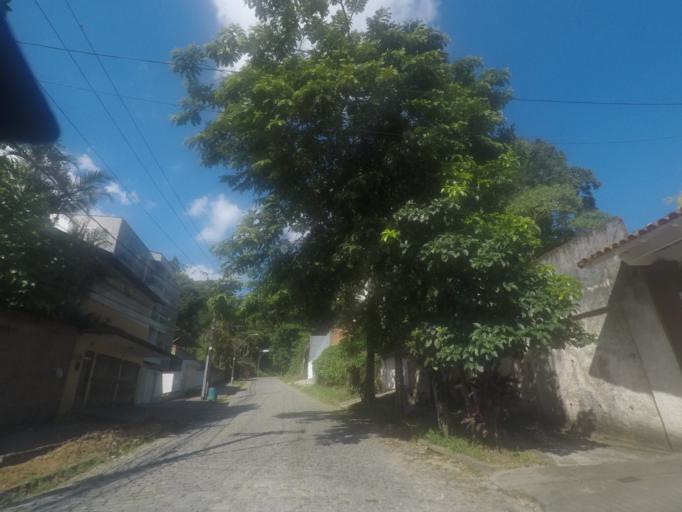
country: BR
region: Rio de Janeiro
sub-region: Petropolis
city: Petropolis
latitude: -22.5238
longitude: -43.2091
